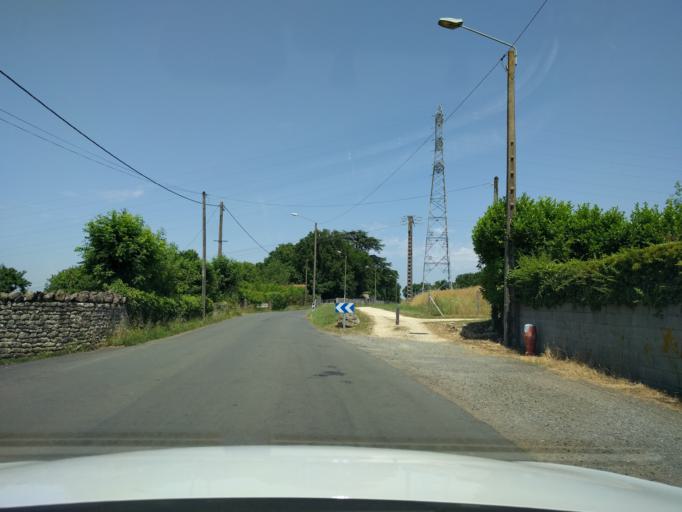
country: FR
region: Poitou-Charentes
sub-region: Departement des Deux-Sevres
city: Niort
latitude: 46.3515
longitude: -0.4536
